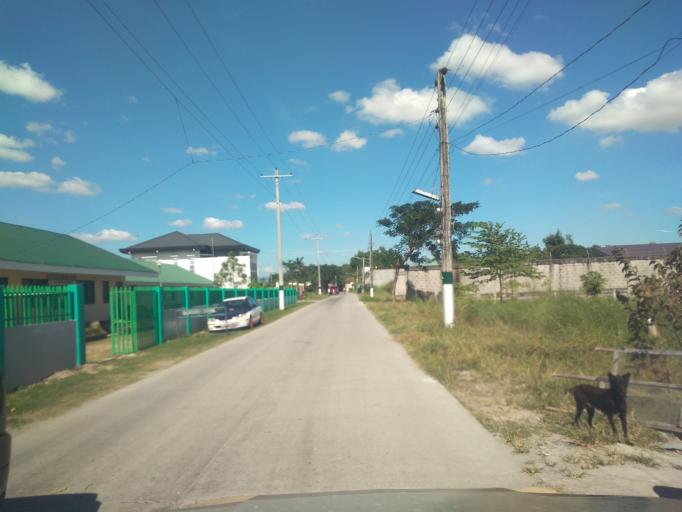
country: PH
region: Central Luzon
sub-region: Province of Pampanga
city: Bacolor
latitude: 15.0154
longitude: 120.6317
